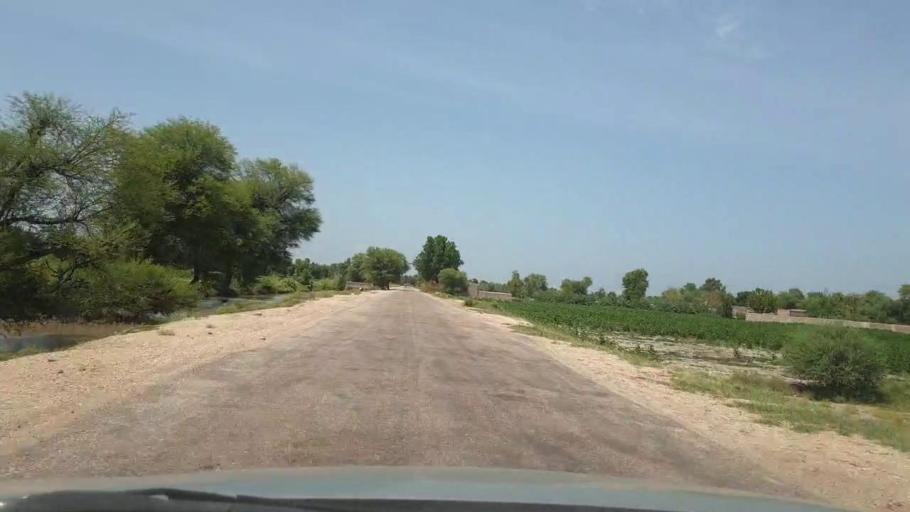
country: PK
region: Sindh
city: Pano Aqil
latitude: 27.6839
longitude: 69.1102
